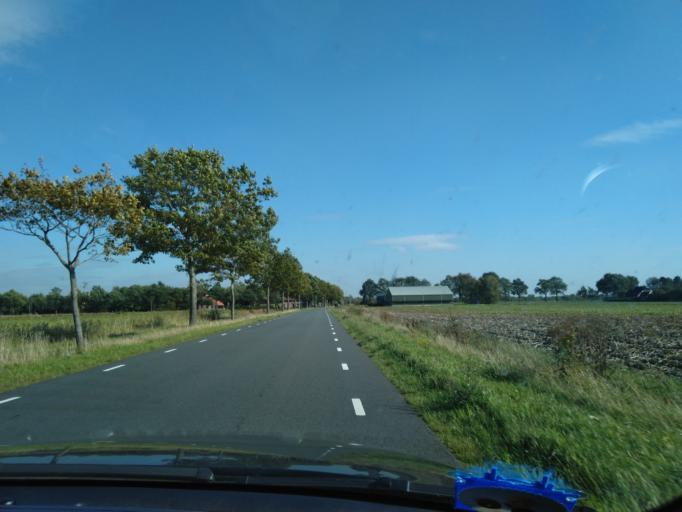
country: NL
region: Groningen
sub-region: Gemeente Veendam
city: Veendam
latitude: 53.0914
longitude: 6.8298
